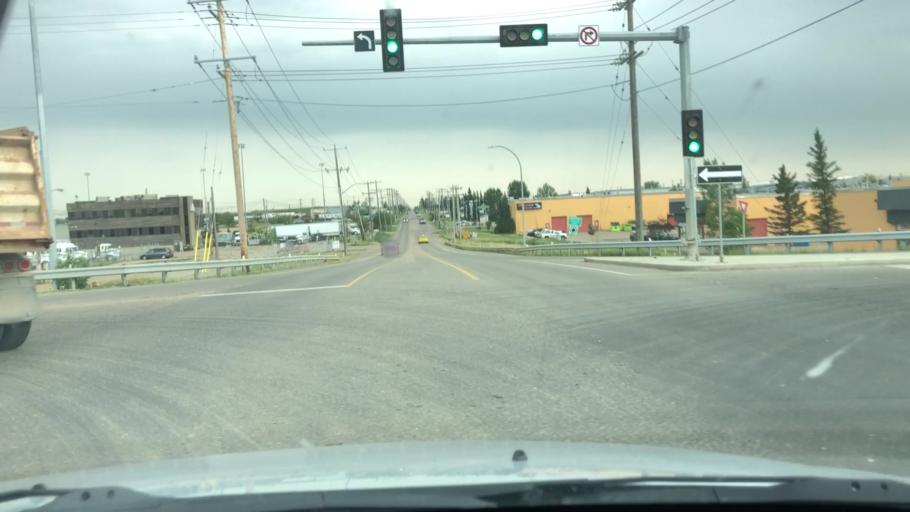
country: CA
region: Alberta
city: Sherwood Park
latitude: 53.5166
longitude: -113.3938
